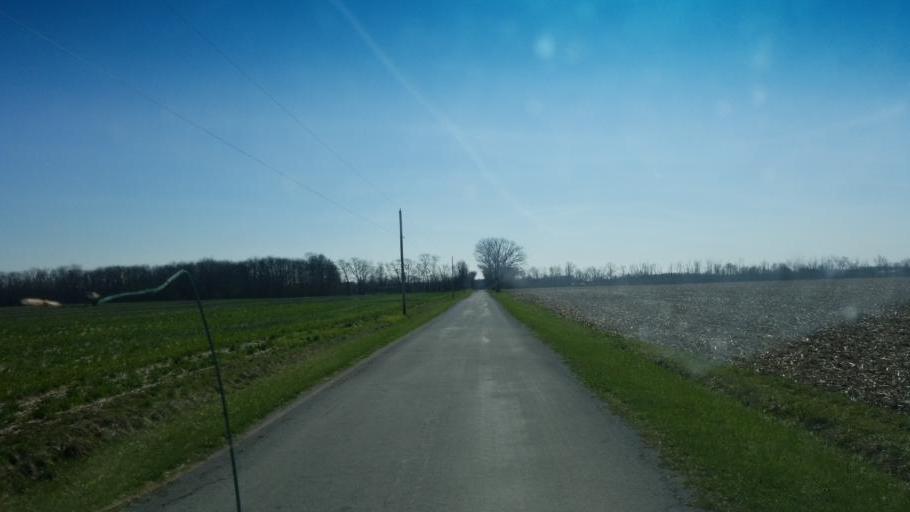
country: US
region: Ohio
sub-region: Hardin County
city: Forest
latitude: 40.7094
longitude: -83.4548
